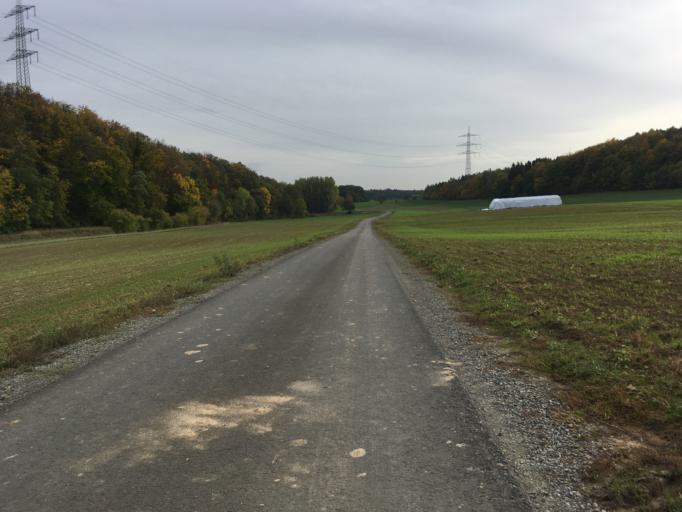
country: DE
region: Baden-Wuerttemberg
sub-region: Karlsruhe Region
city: Buchen
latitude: 49.4867
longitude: 9.3420
